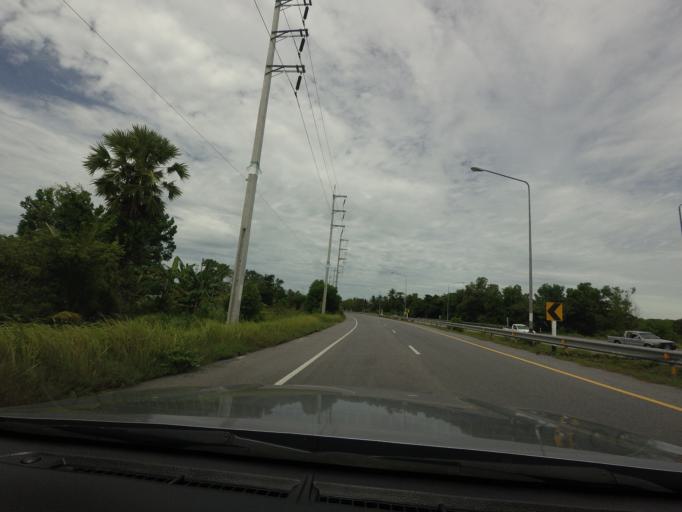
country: TH
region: Pattani
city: Nong Chik
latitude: 6.8299
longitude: 101.2169
